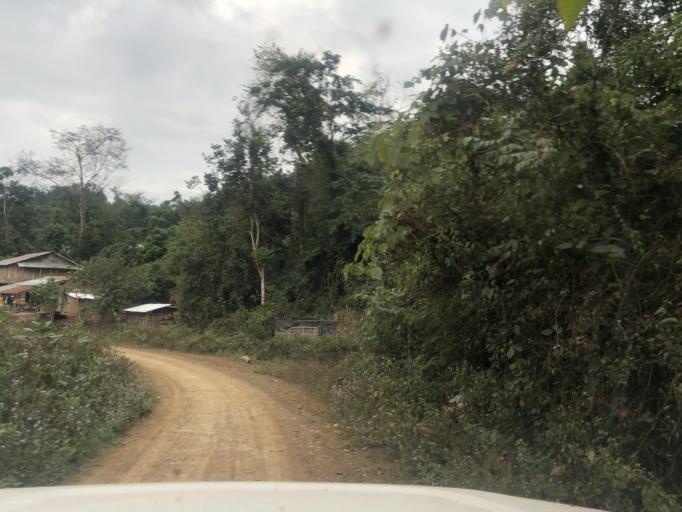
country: LA
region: Phongsali
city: Khoa
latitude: 21.3033
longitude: 102.5839
